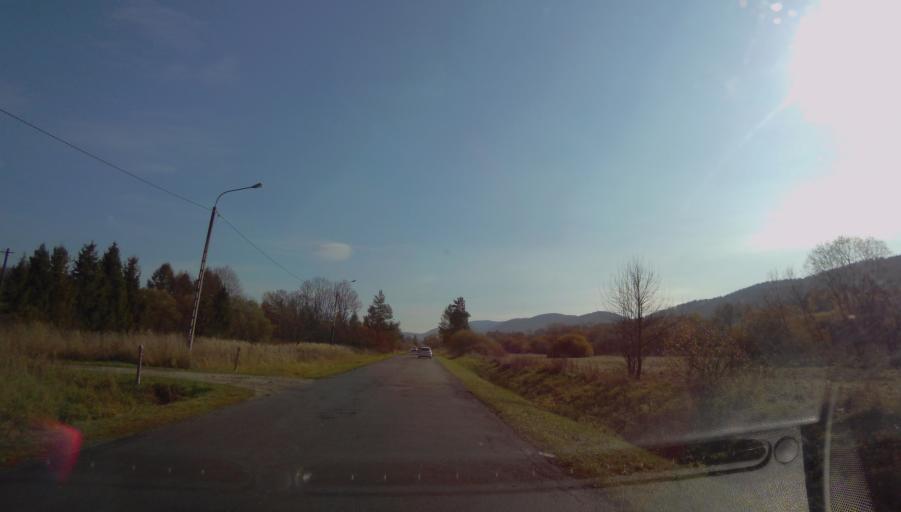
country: PL
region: Subcarpathian Voivodeship
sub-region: Powiat sanocki
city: Rzepedz
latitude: 49.2299
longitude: 22.1637
